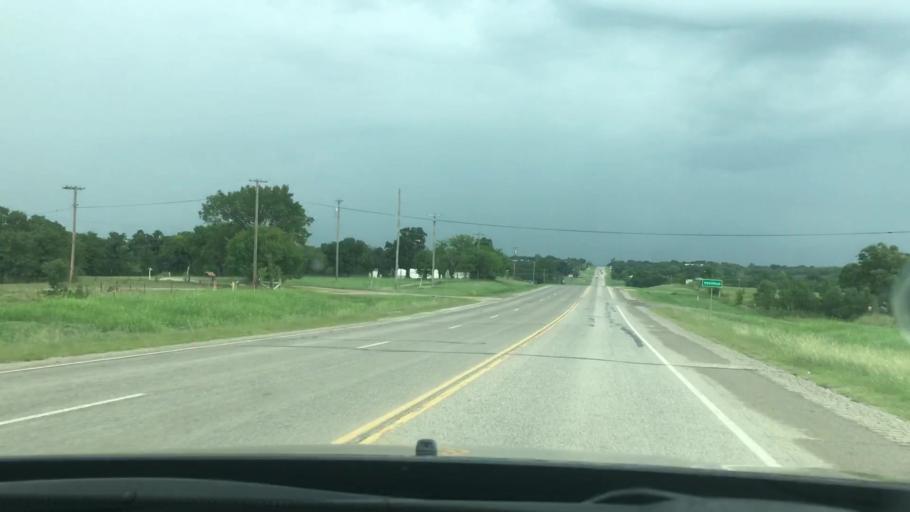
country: US
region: Oklahoma
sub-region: Carter County
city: Healdton
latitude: 34.2010
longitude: -97.4747
